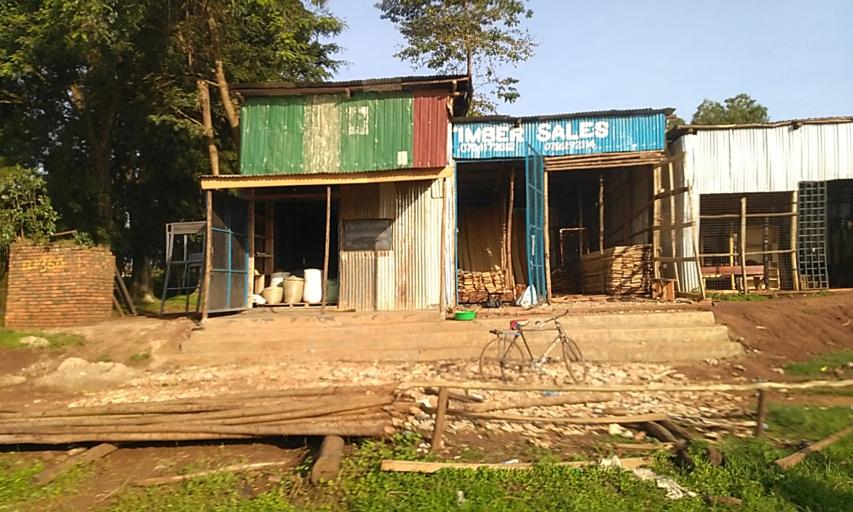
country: UG
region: Central Region
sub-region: Wakiso District
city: Kireka
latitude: 0.4420
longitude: 32.6070
